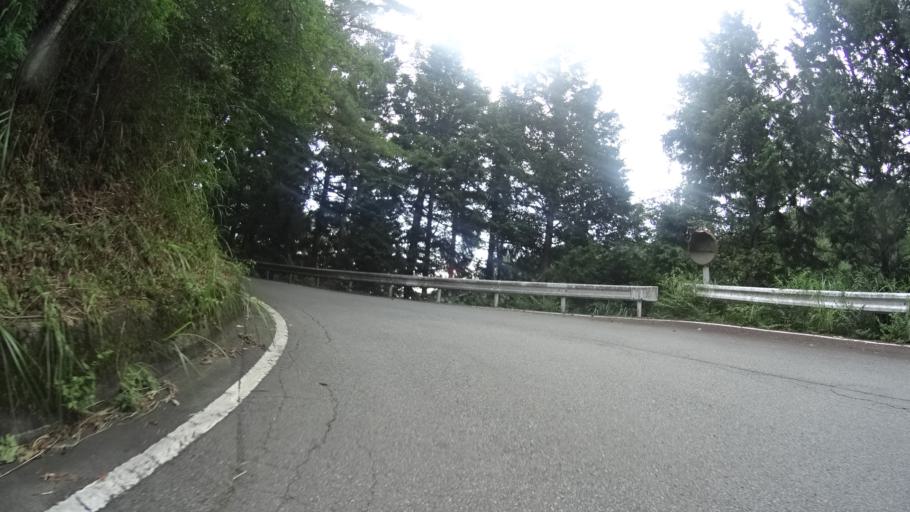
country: JP
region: Yamanashi
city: Enzan
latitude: 35.7917
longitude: 138.6832
